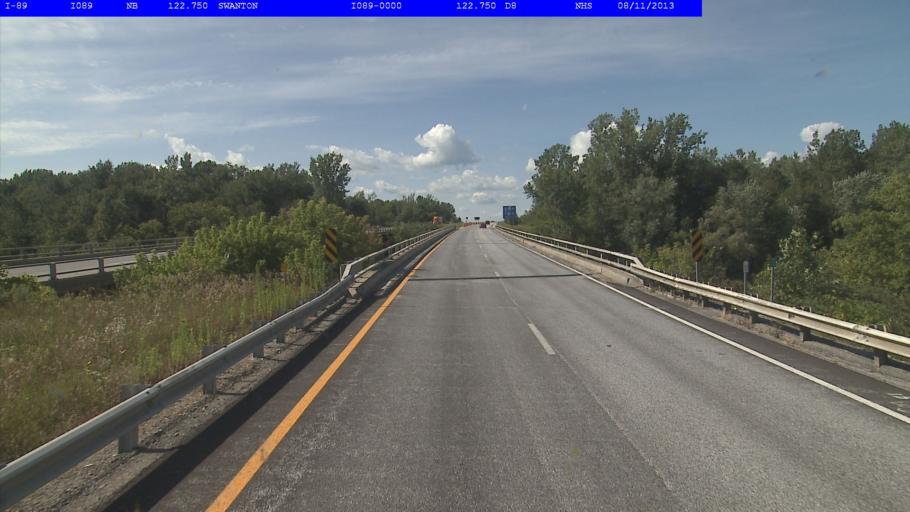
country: US
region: Vermont
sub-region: Franklin County
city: Swanton
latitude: 44.9138
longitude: -73.1029
